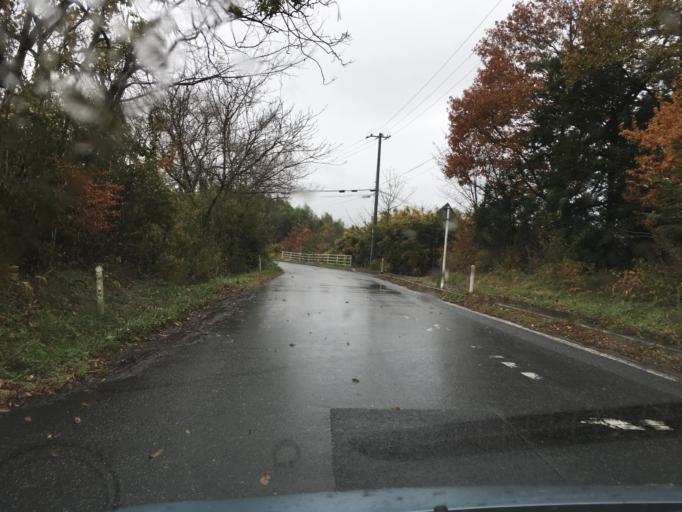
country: JP
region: Iwate
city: Ichinoseki
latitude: 38.7877
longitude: 141.2318
